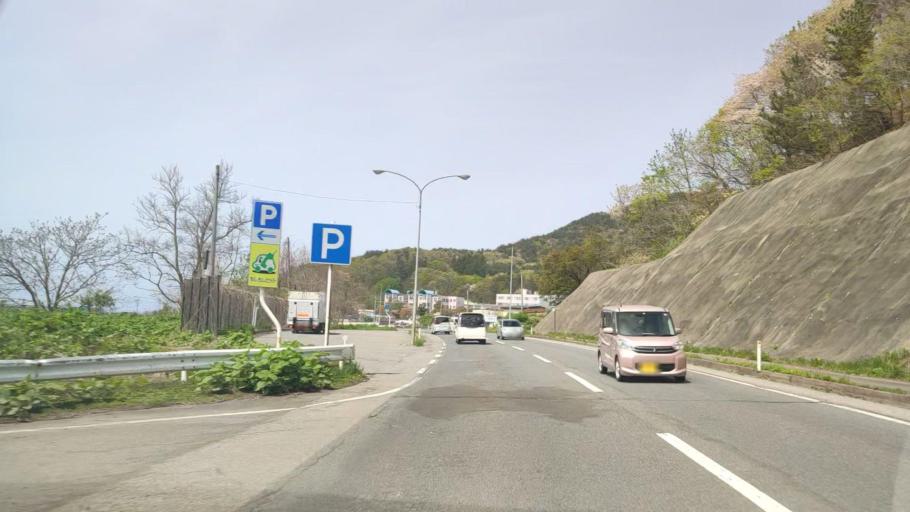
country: JP
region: Aomori
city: Aomori Shi
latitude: 40.8739
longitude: 140.8516
